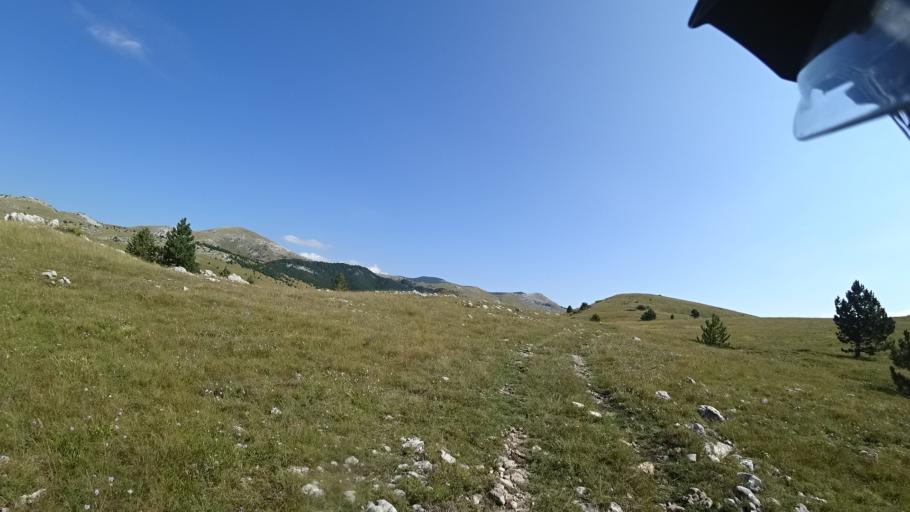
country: HR
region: Zadarska
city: Gracac
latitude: 44.3108
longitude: 15.9970
